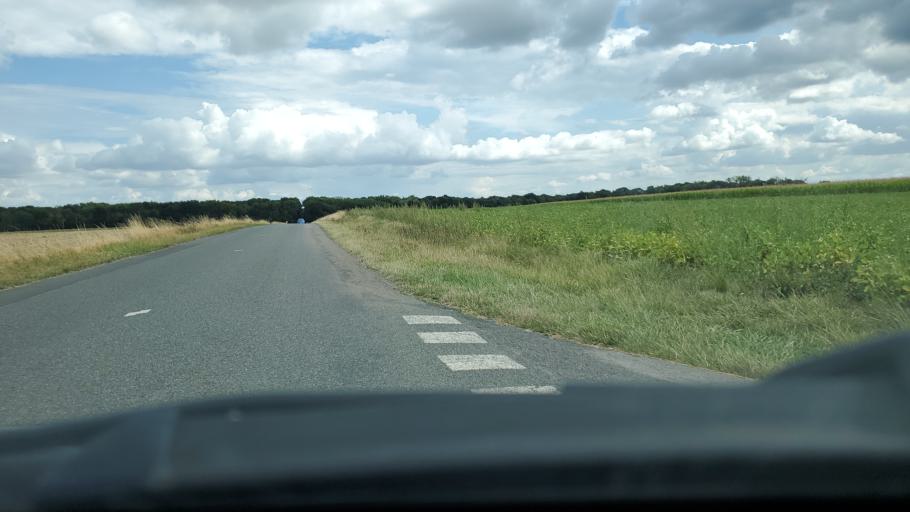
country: FR
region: Ile-de-France
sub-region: Departement de Seine-et-Marne
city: Pommeuse
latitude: 48.8642
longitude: 3.0019
